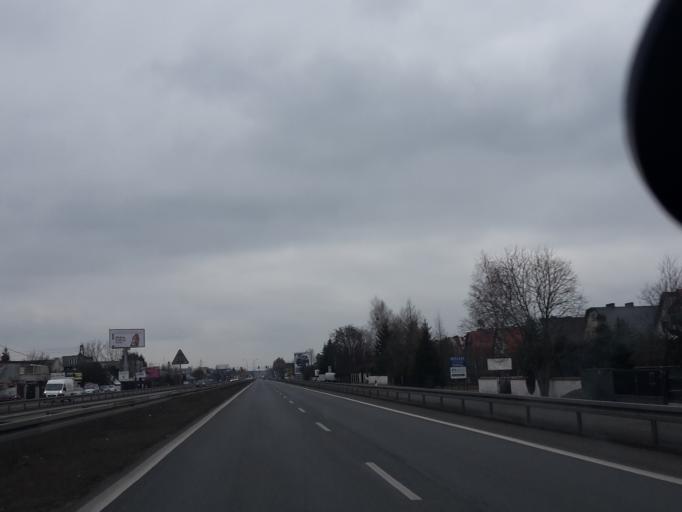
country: PL
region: Masovian Voivodeship
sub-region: Powiat warszawski zachodni
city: Lomianki
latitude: 52.3377
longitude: 20.8758
